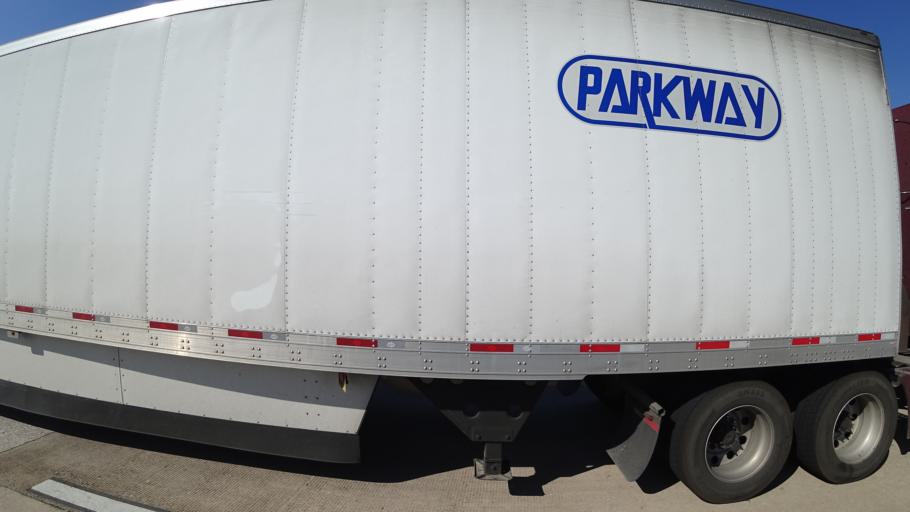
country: US
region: Texas
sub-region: Travis County
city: Hornsby Bend
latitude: 30.2293
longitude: -97.6193
